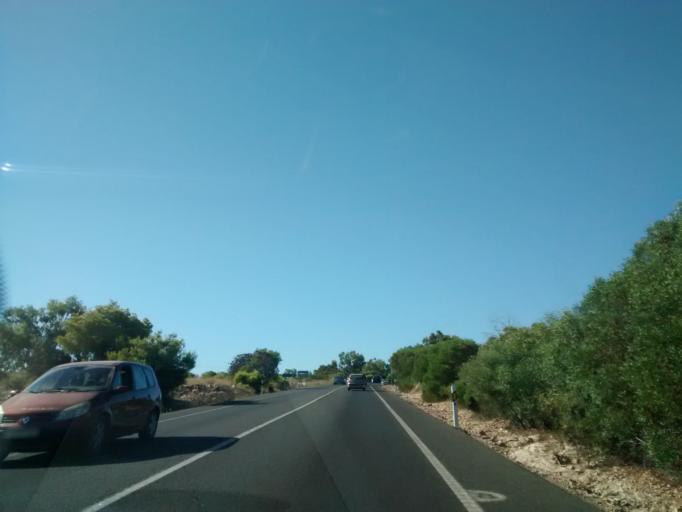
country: ES
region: Valencia
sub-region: Provincia de Alicante
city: Santa Pola
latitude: 38.2240
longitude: -0.5537
